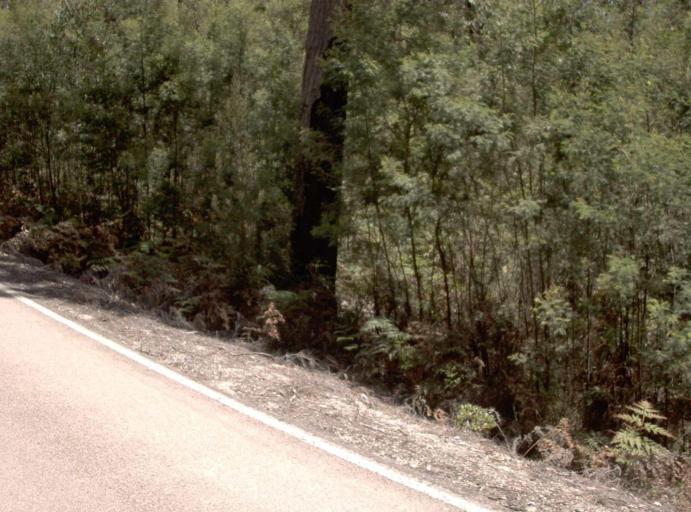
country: AU
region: Victoria
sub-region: East Gippsland
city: Lakes Entrance
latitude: -37.6497
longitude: 147.8923
